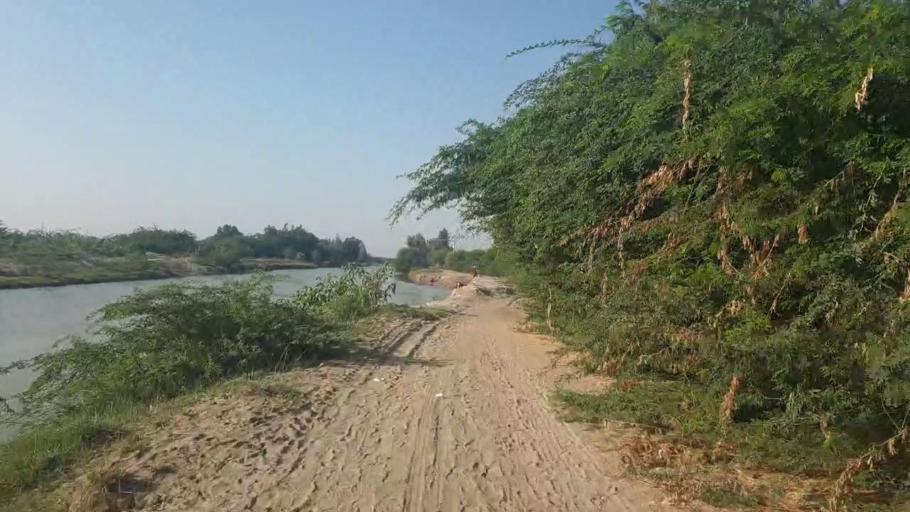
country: PK
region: Sindh
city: Tando Bago
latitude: 24.7305
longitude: 68.9289
